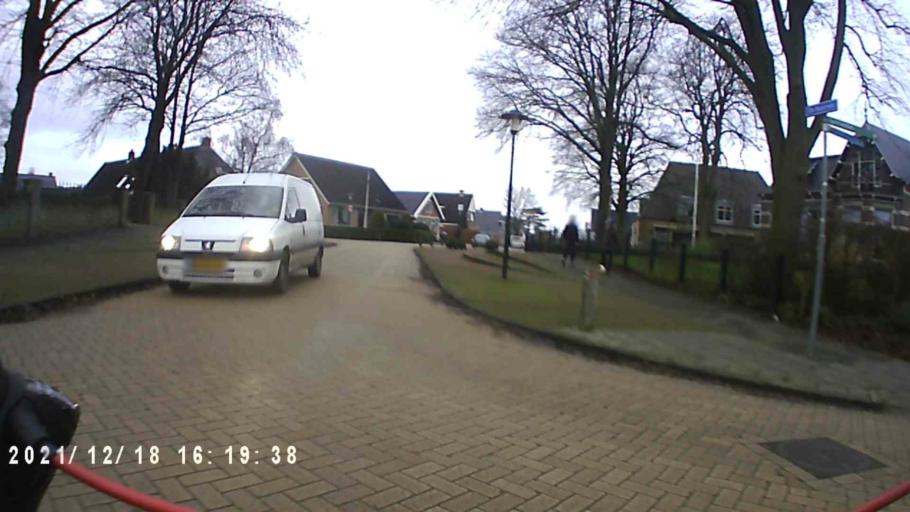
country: NL
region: Friesland
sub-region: Gemeente Dongeradeel
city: Anjum
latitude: 53.3787
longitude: 6.0539
